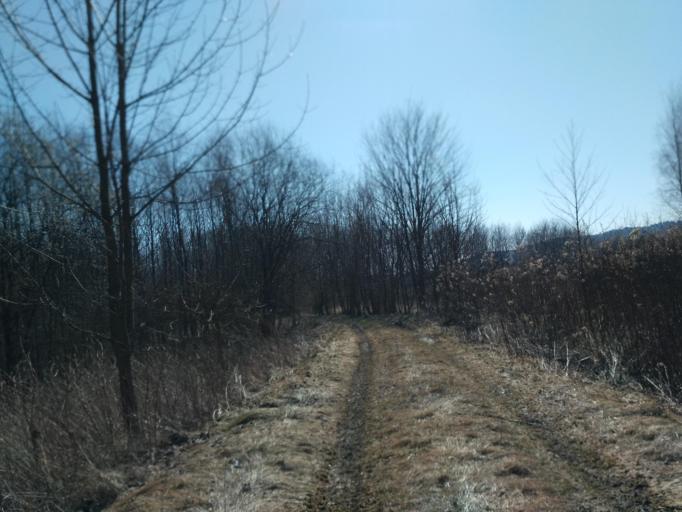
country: PL
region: Subcarpathian Voivodeship
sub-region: Powiat brzozowski
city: Domaradz
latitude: 49.7984
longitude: 21.9683
